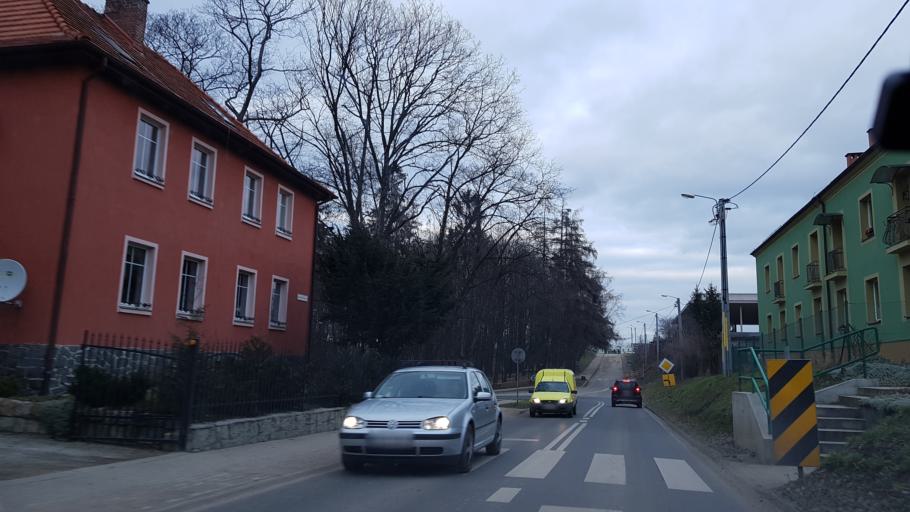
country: PL
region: Lower Silesian Voivodeship
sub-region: Powiat zabkowicki
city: Zabkowice Slaskie
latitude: 50.5917
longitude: 16.8227
